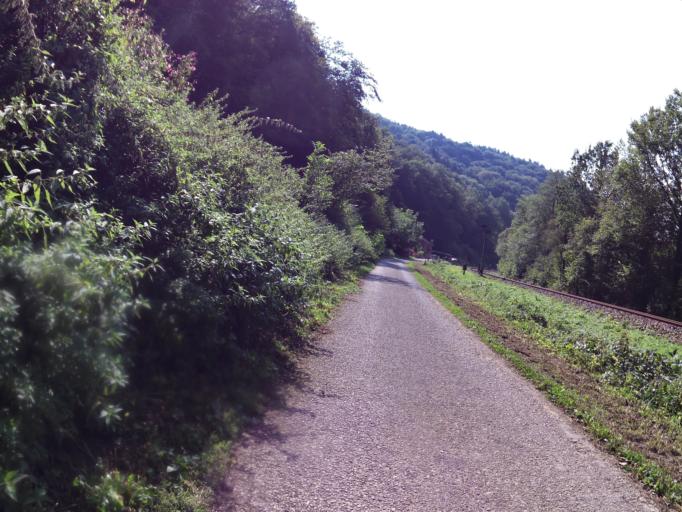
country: DE
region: Rheinland-Pfalz
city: Hosten
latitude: 49.8930
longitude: 6.6071
